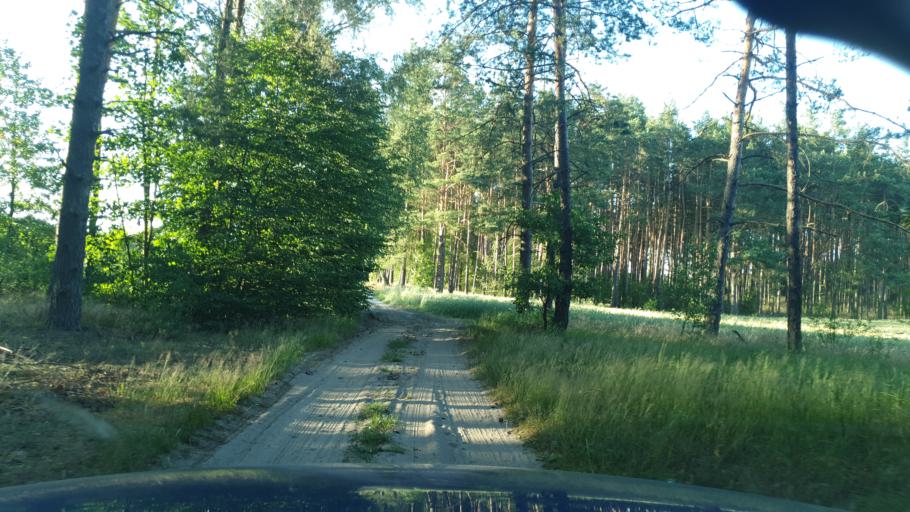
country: PL
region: Pomeranian Voivodeship
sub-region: Powiat bytowski
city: Lipnica
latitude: 53.8813
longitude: 17.4267
